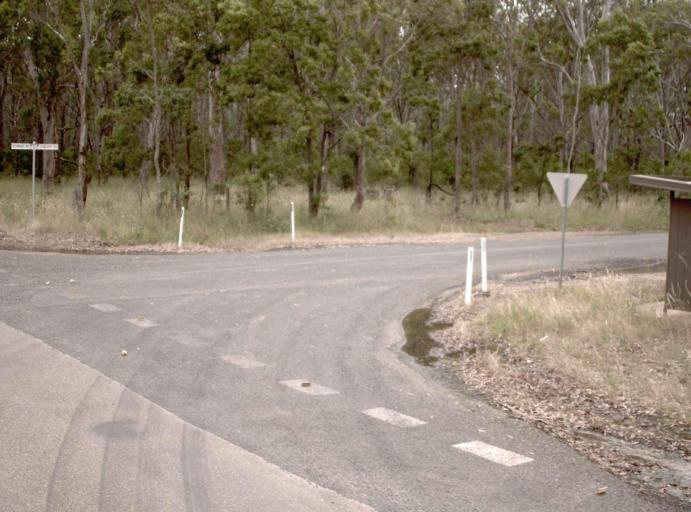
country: AU
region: Victoria
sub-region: Wellington
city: Sale
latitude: -37.8549
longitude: 147.0704
